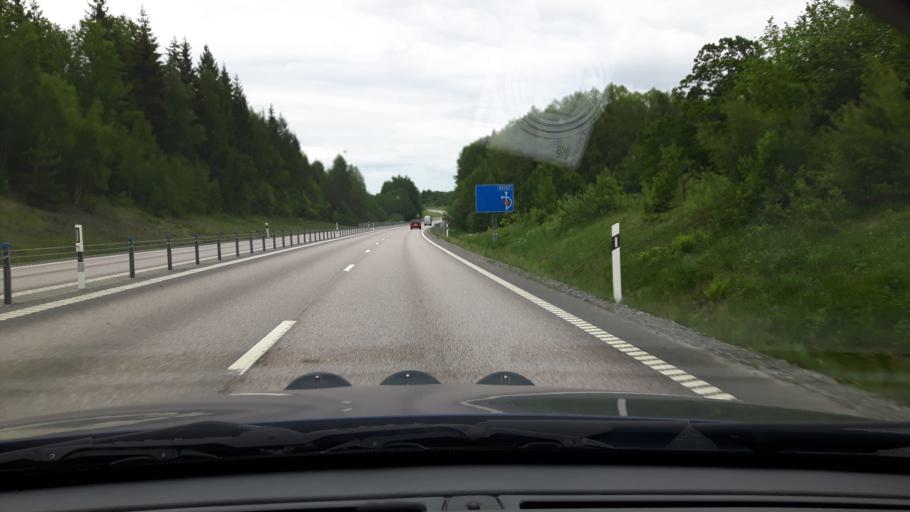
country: SE
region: Soedermanland
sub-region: Flens Kommun
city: Flen
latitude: 59.0378
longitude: 16.5533
